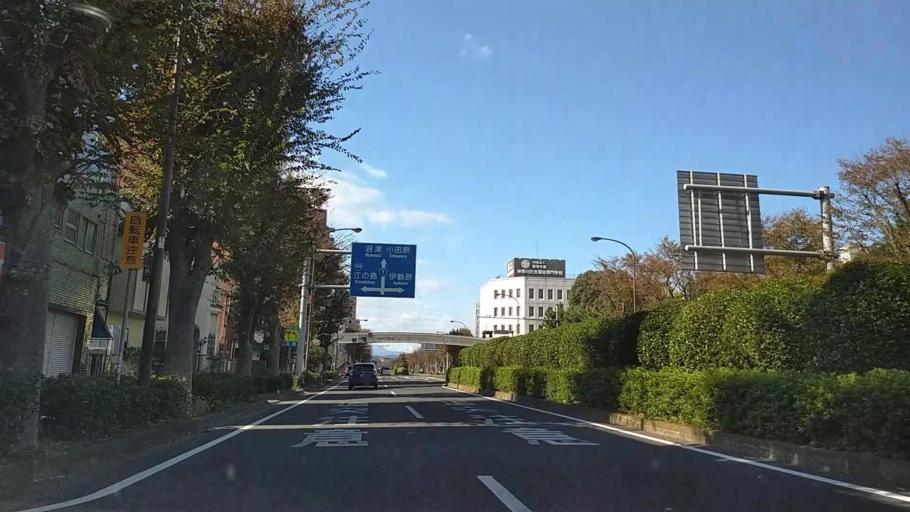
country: JP
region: Kanagawa
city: Hiratsuka
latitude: 35.3325
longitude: 139.3453
